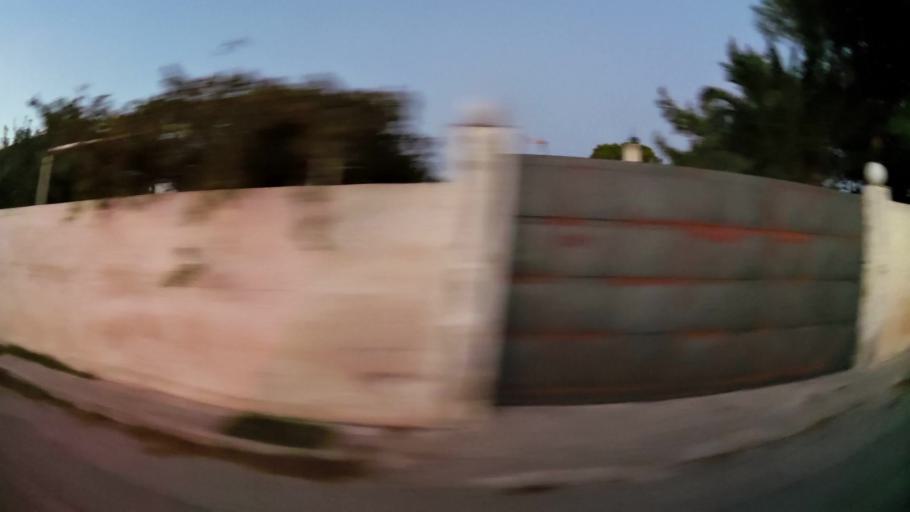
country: GR
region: Attica
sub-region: Nomarchia Anatolikis Attikis
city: Agia Marina
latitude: 37.8233
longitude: 23.8558
